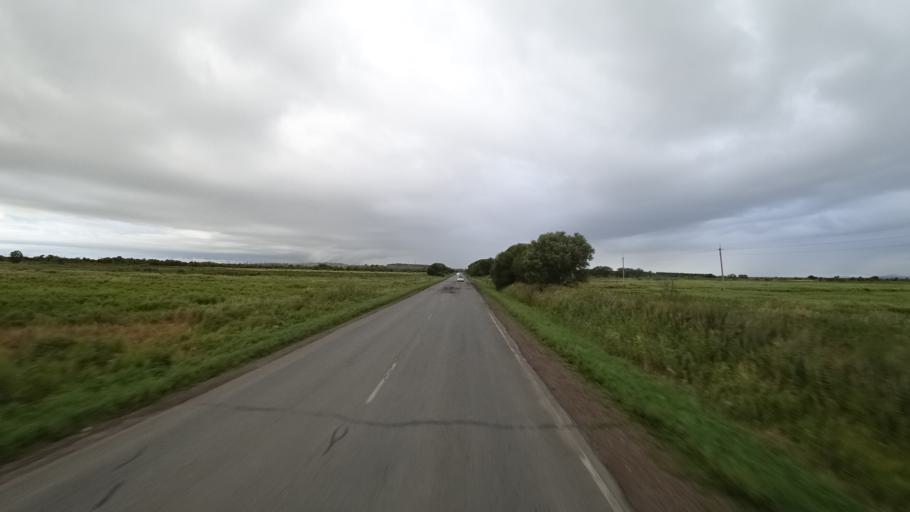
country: RU
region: Primorskiy
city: Chernigovka
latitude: 44.3580
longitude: 132.5596
